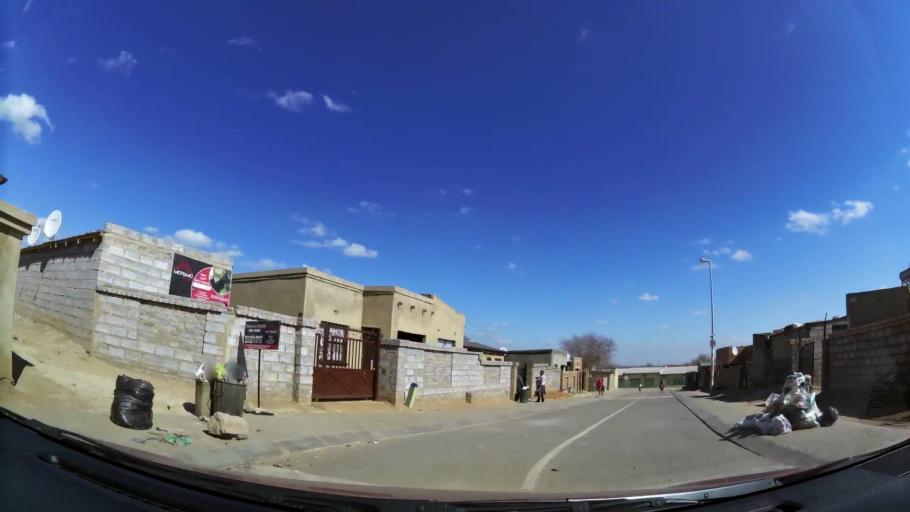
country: ZA
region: Gauteng
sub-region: City of Johannesburg Metropolitan Municipality
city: Modderfontein
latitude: -26.0333
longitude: 28.1731
